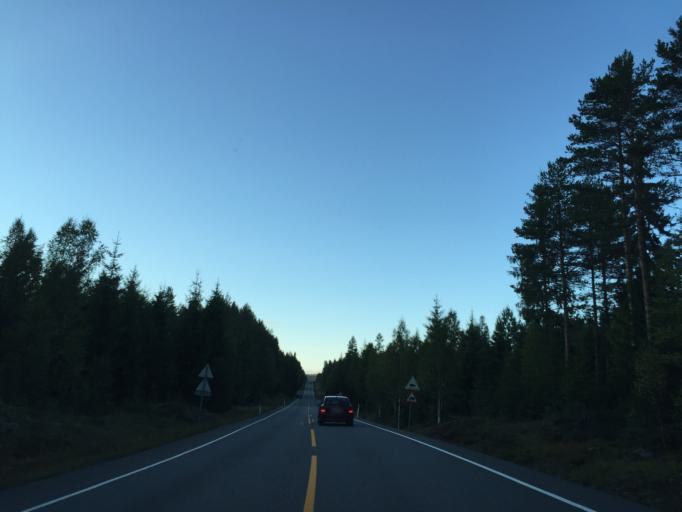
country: NO
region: Hedmark
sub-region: Nord-Odal
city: Sand
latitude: 60.5184
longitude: 11.5114
